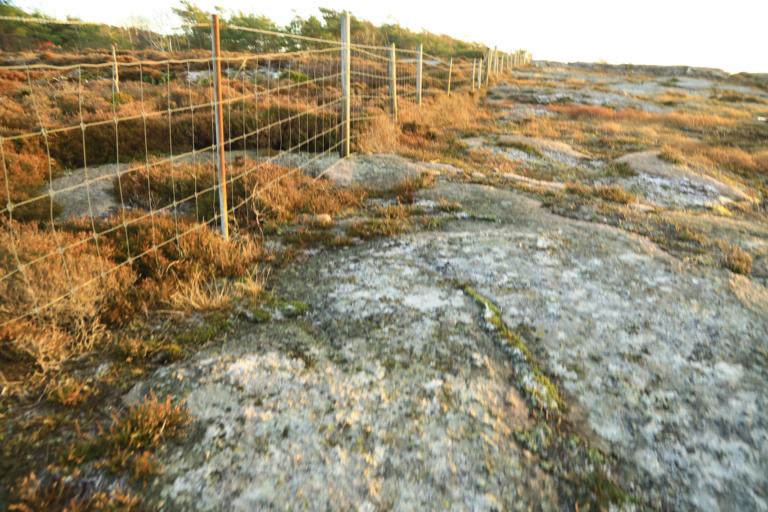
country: SE
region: Halland
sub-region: Varbergs Kommun
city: Varberg
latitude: 57.1921
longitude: 12.1619
